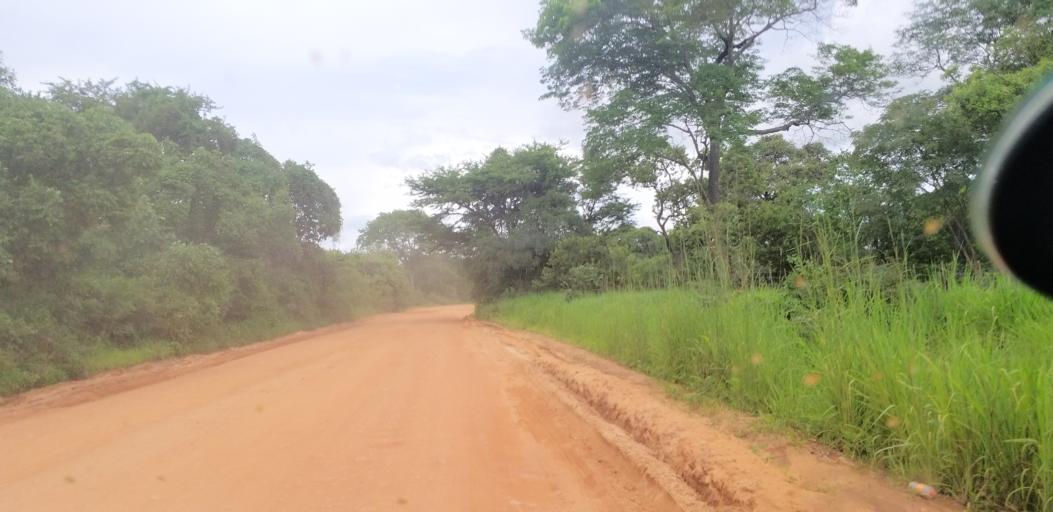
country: ZM
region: Lusaka
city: Lusaka
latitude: -15.1997
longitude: 28.4399
